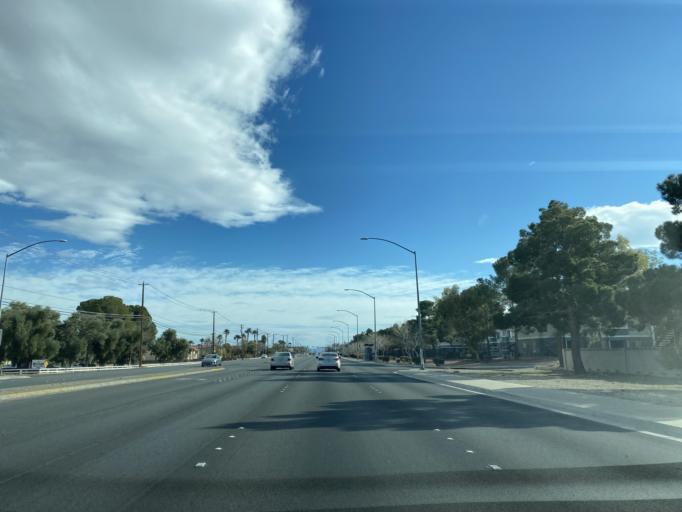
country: US
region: Nevada
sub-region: Clark County
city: Las Vegas
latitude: 36.2277
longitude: -115.2219
